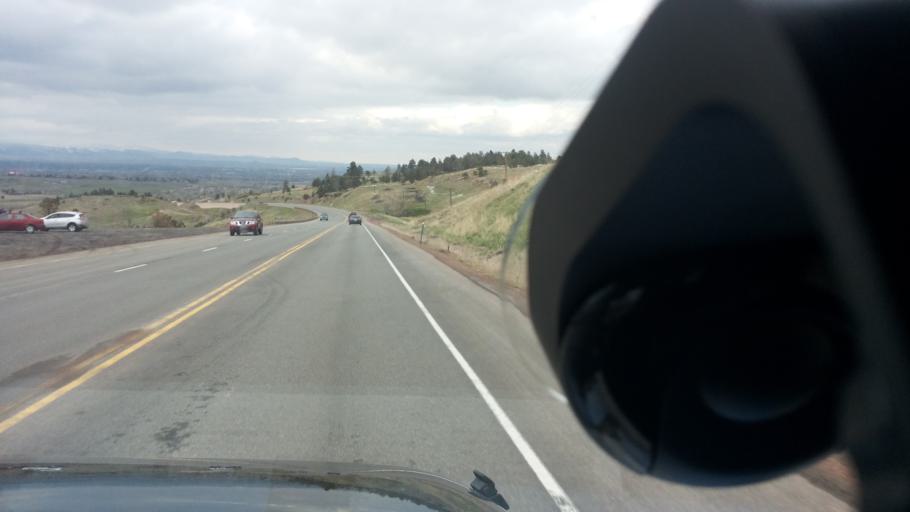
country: US
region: Colorado
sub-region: Boulder County
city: Superior
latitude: 39.9381
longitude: -105.2364
